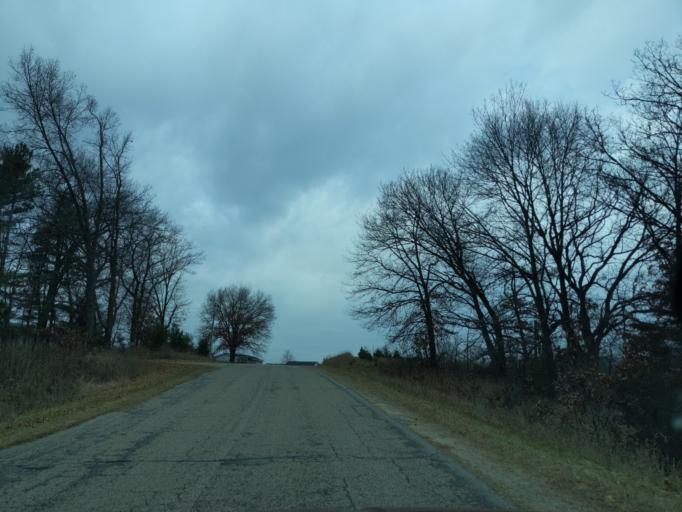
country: US
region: Wisconsin
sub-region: Waushara County
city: Wautoma
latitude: 44.0507
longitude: -89.2774
